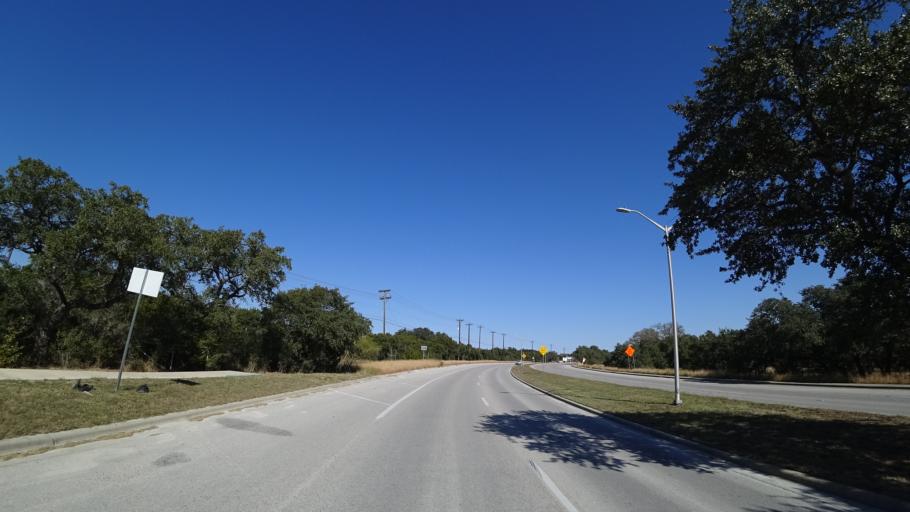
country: US
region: Texas
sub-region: Williamson County
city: Cedar Park
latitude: 30.4910
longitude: -97.8606
